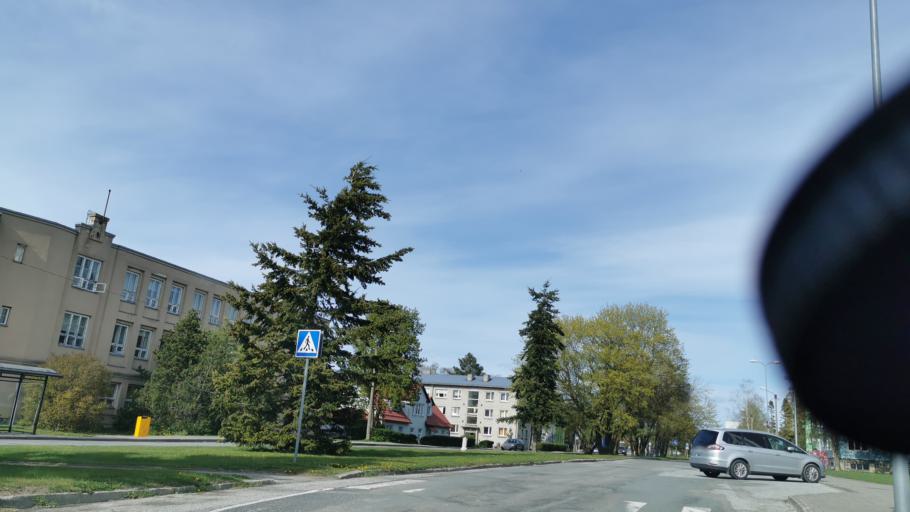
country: EE
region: Laeaene-Virumaa
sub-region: Rakvere linn
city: Rakvere
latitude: 59.3441
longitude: 26.3639
